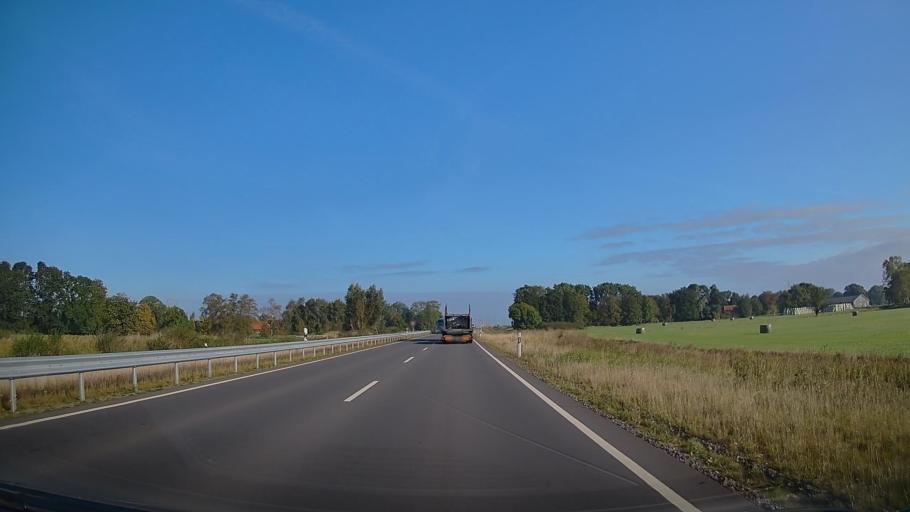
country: DE
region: Lower Saxony
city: Ovelgonne
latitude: 53.3060
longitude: 8.3975
